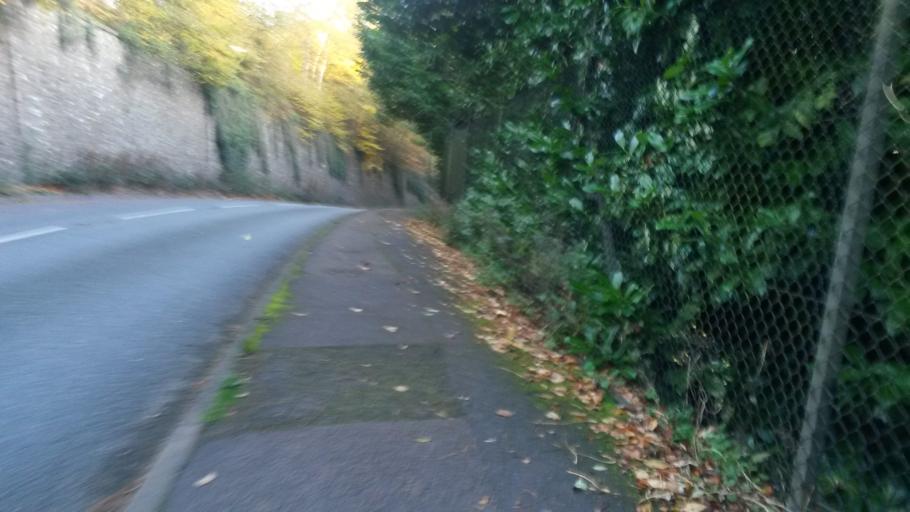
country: GB
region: England
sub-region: Surrey
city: Haslemere
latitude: 51.0840
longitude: -0.7318
